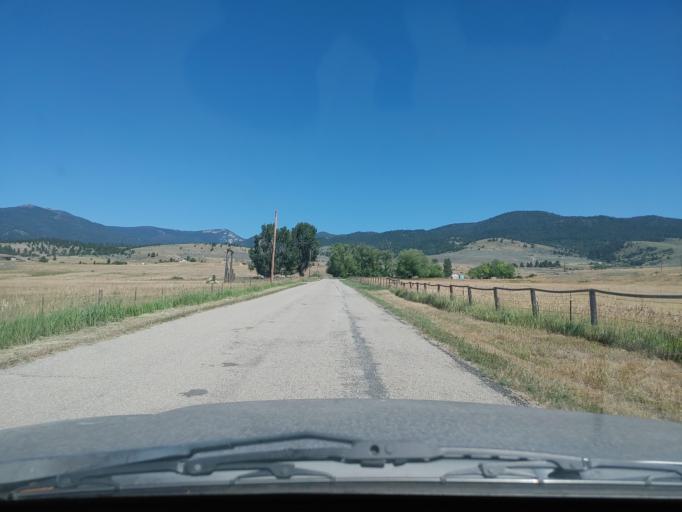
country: US
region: Montana
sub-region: Ravalli County
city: Hamilton
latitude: 46.2767
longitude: -114.0330
